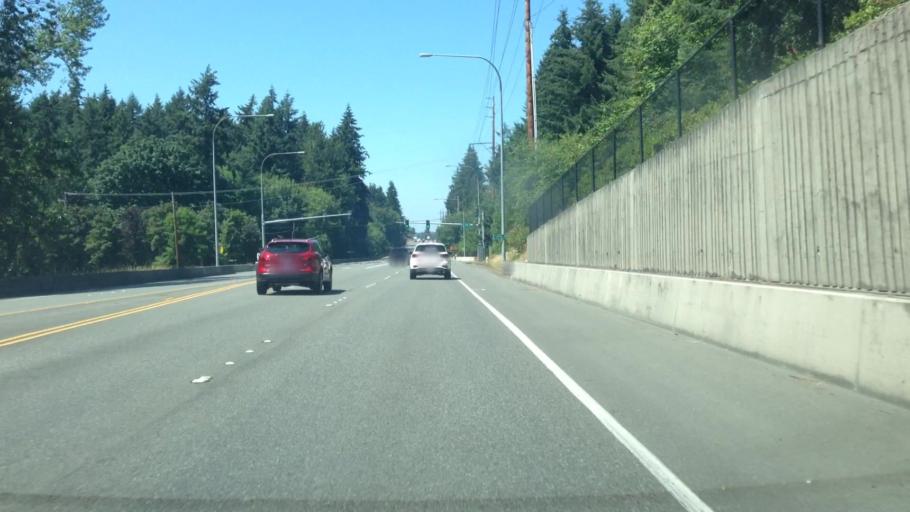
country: US
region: Washington
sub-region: King County
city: Lakeland South
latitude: 47.2716
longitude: -122.3050
